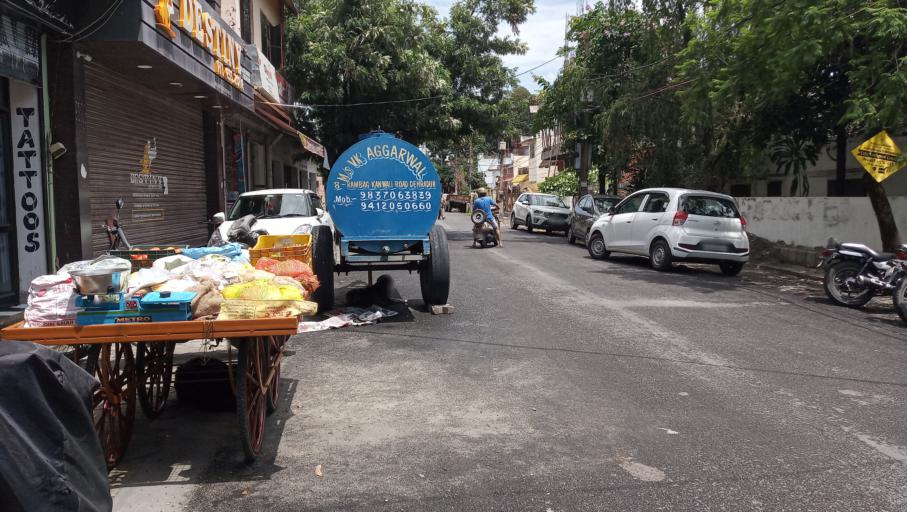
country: IN
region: Uttarakhand
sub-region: Dehradun
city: Dehradun
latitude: 30.3648
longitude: 78.0677
